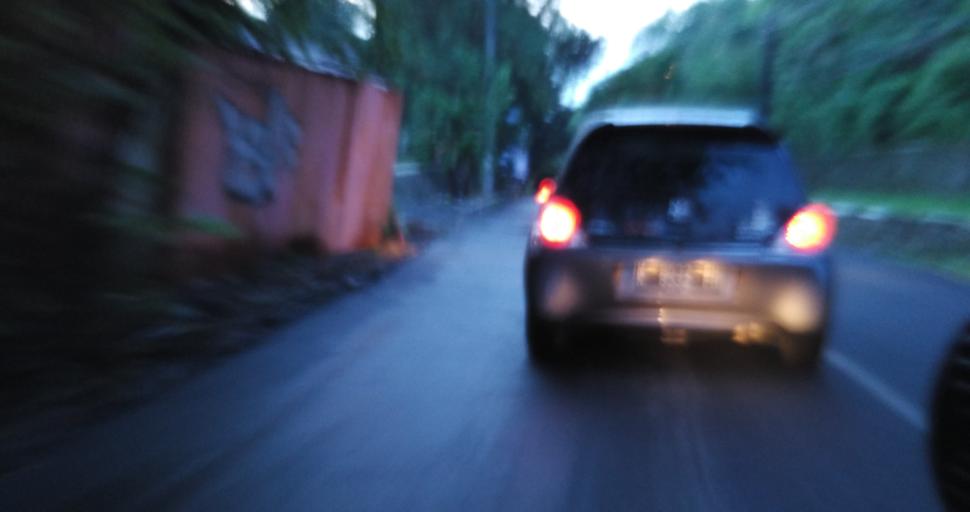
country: ID
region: Central Java
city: Semarang
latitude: -7.0428
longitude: 110.4215
